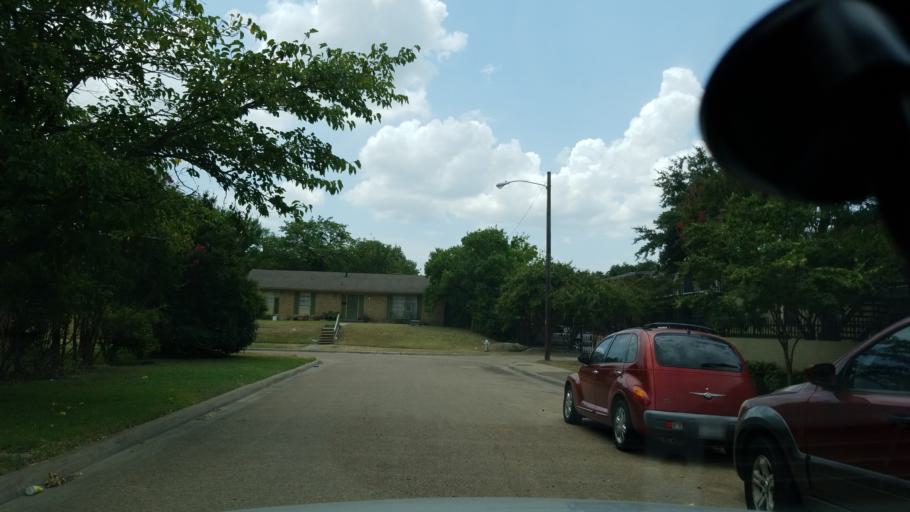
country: US
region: Texas
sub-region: Dallas County
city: Cockrell Hill
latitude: 32.6922
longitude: -96.8537
